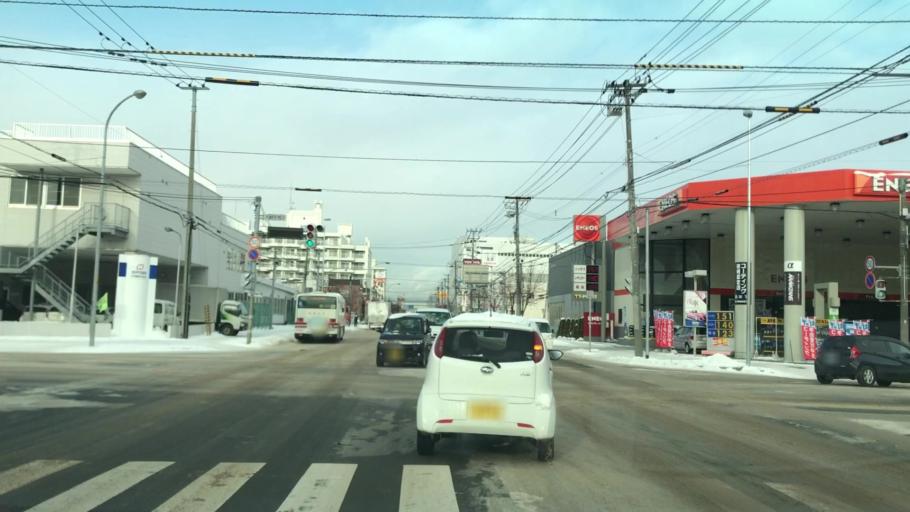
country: JP
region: Hokkaido
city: Sapporo
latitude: 43.0938
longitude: 141.3037
